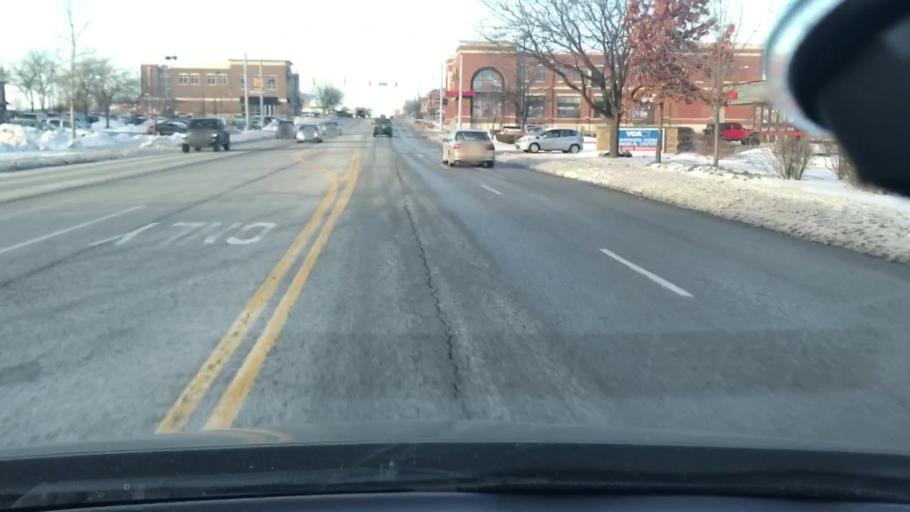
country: US
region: Indiana
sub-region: Hamilton County
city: Carmel
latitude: 39.9574
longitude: -86.1267
